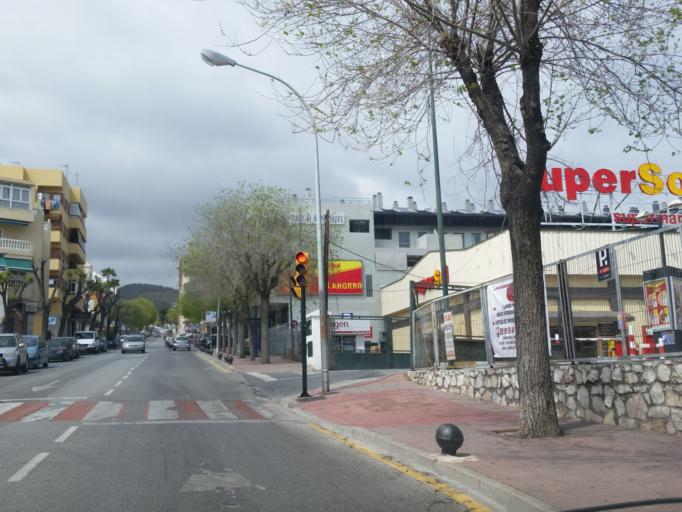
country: ES
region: Andalusia
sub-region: Provincia de Malaga
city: Benalmadena
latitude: 36.6004
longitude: -4.5320
